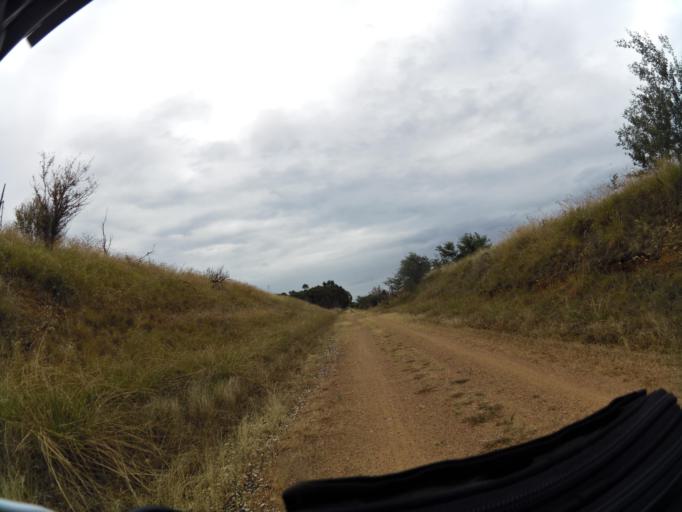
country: AU
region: New South Wales
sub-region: Albury Municipality
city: East Albury
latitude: -36.2146
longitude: 147.0570
